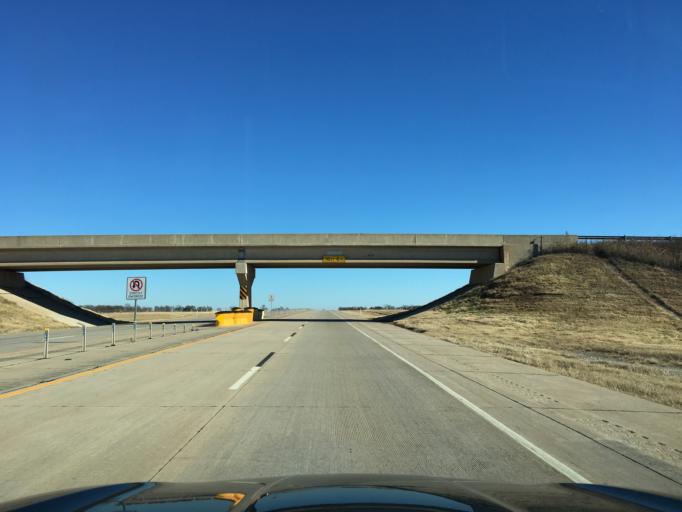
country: US
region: Oklahoma
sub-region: Payne County
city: Yale
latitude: 36.2250
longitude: -96.6607
